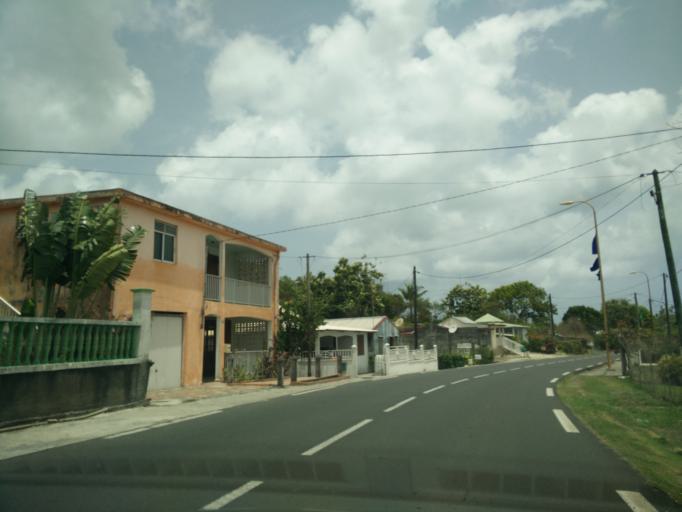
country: GP
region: Guadeloupe
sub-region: Guadeloupe
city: Port-Louis
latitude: 16.4151
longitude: -61.5246
